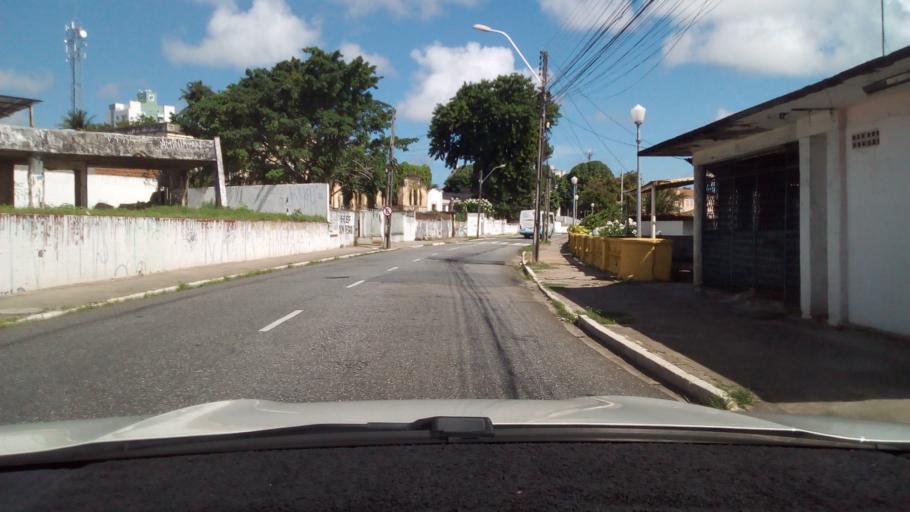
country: BR
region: Paraiba
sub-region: Joao Pessoa
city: Joao Pessoa
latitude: -7.1304
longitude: -34.8823
